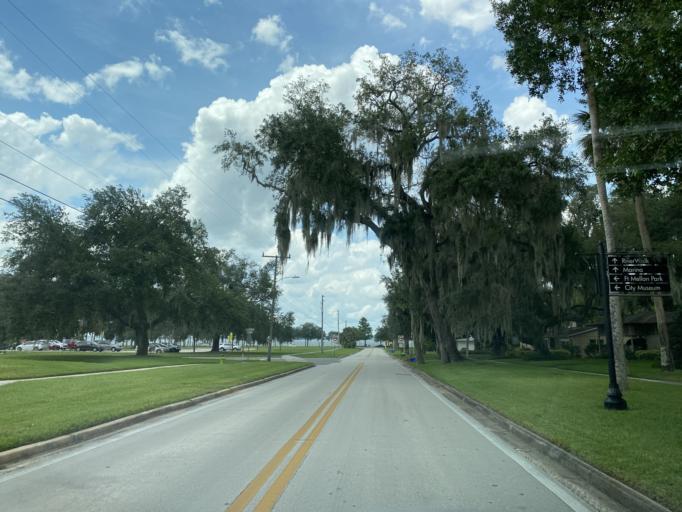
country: US
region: Florida
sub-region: Seminole County
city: Sanford
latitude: 28.8108
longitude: -81.2549
